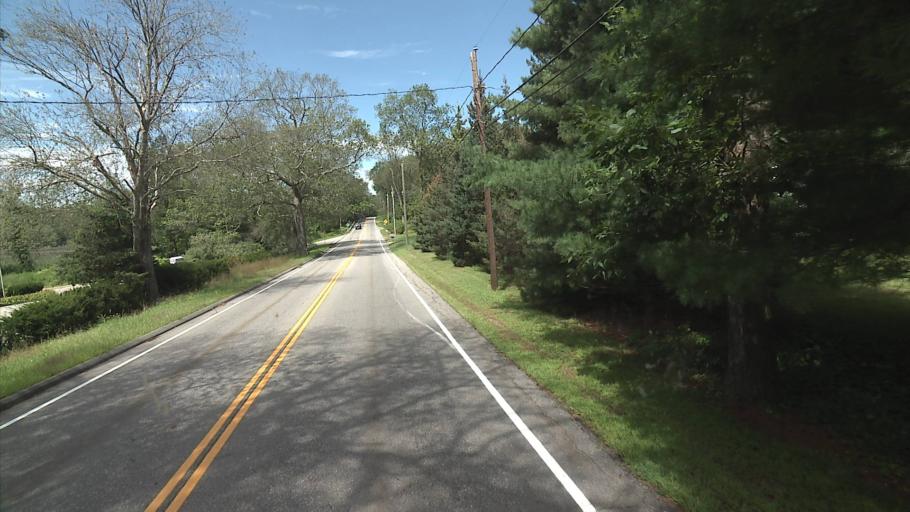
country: US
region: Connecticut
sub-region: Tolland County
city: Mansfield City
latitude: 41.7744
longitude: -72.2073
